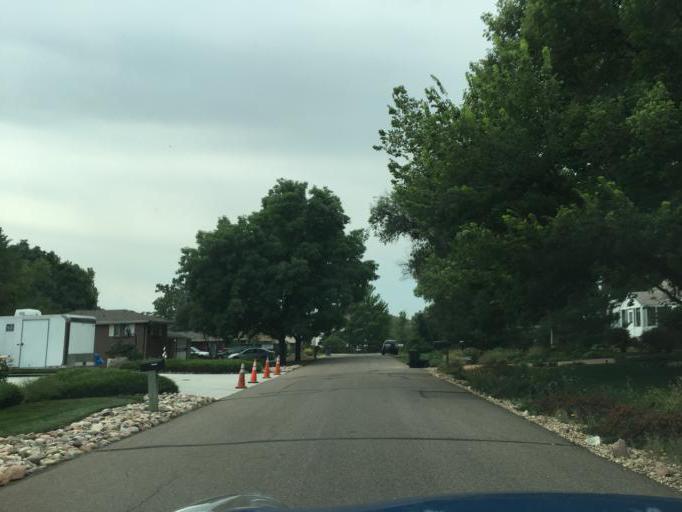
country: US
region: Colorado
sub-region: Jefferson County
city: Wheat Ridge
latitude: 39.7459
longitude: -105.0944
